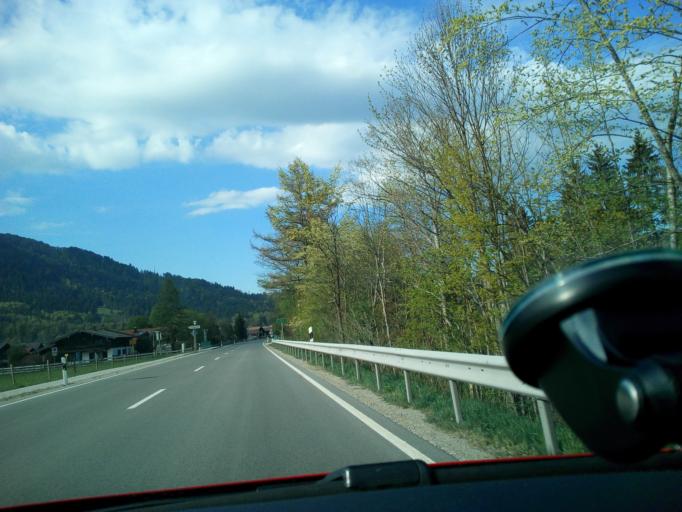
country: DE
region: Bavaria
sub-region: Upper Bavaria
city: Kreuth
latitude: 47.6588
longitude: 11.7494
